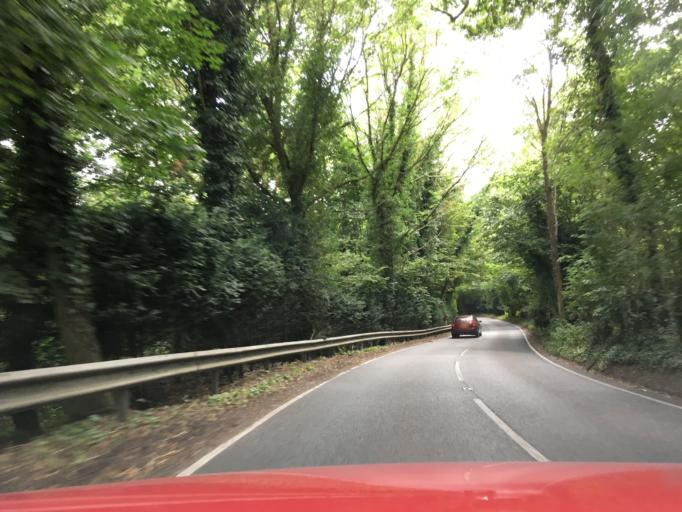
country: GB
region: England
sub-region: East Sussex
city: Crowborough
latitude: 51.1233
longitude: 0.1943
